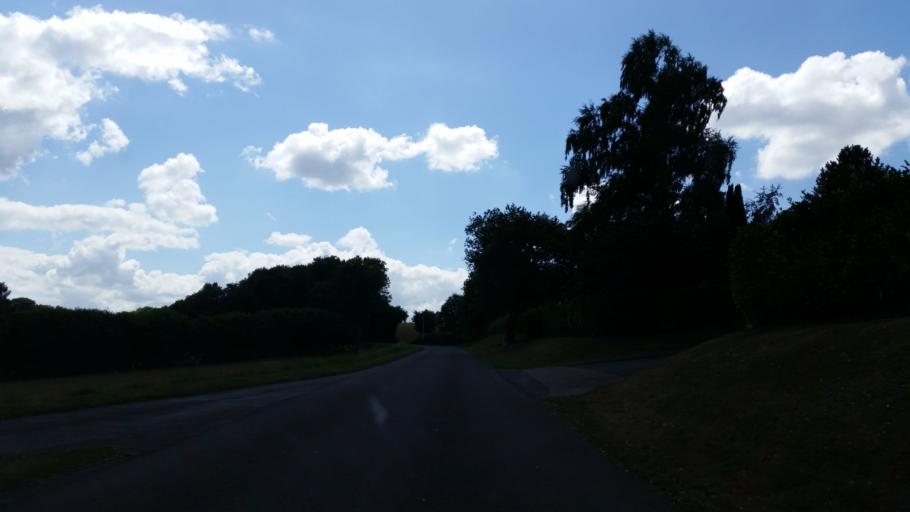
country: FR
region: Lower Normandy
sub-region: Departement du Calvados
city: Clecy
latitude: 48.8369
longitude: -0.3785
